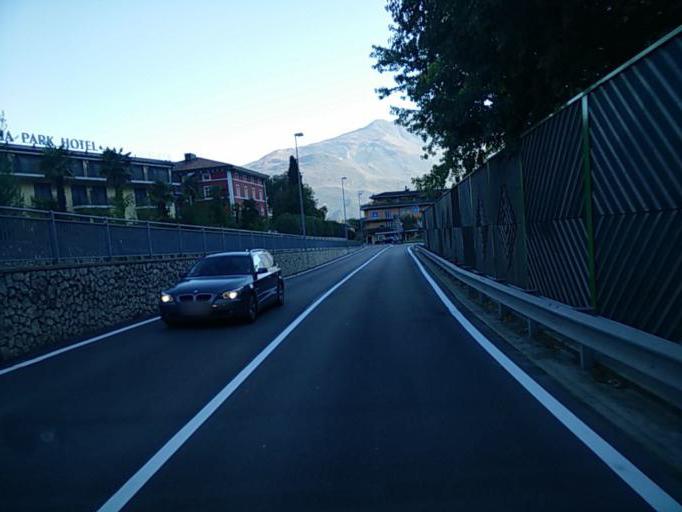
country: IT
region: Trentino-Alto Adige
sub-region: Provincia di Trento
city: Riva del Garda
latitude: 45.8931
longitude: 10.8458
